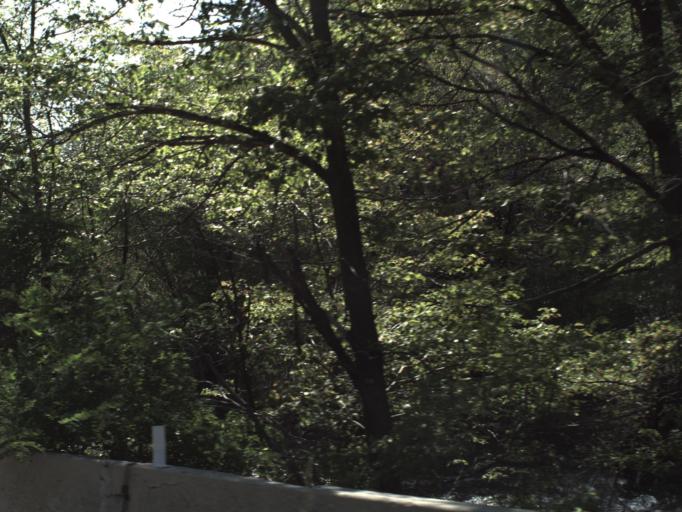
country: US
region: Utah
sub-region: Weber County
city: Ogden
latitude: 41.2437
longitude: -111.8941
